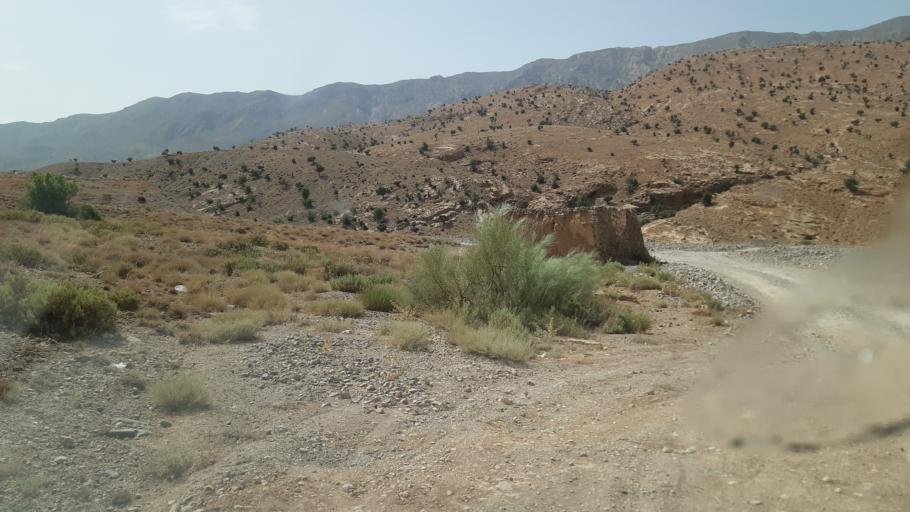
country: MA
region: Meknes-Tafilalet
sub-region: Khenifra
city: Midelt
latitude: 32.5838
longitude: -4.7672
